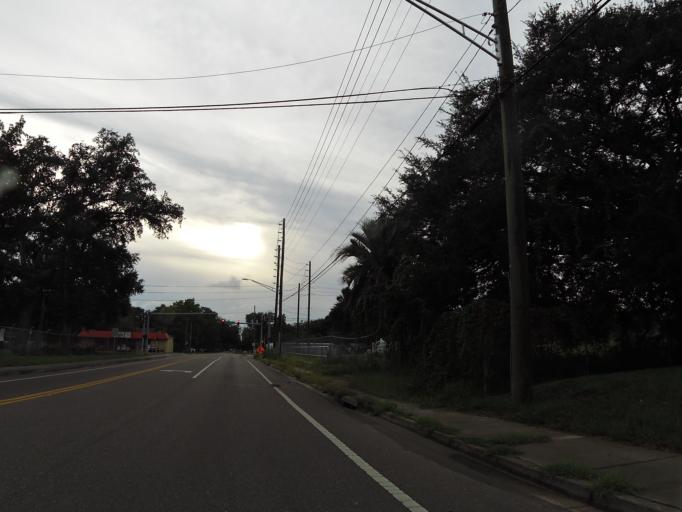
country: US
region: Florida
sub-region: Duval County
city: Jacksonville
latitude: 30.3439
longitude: -81.7132
